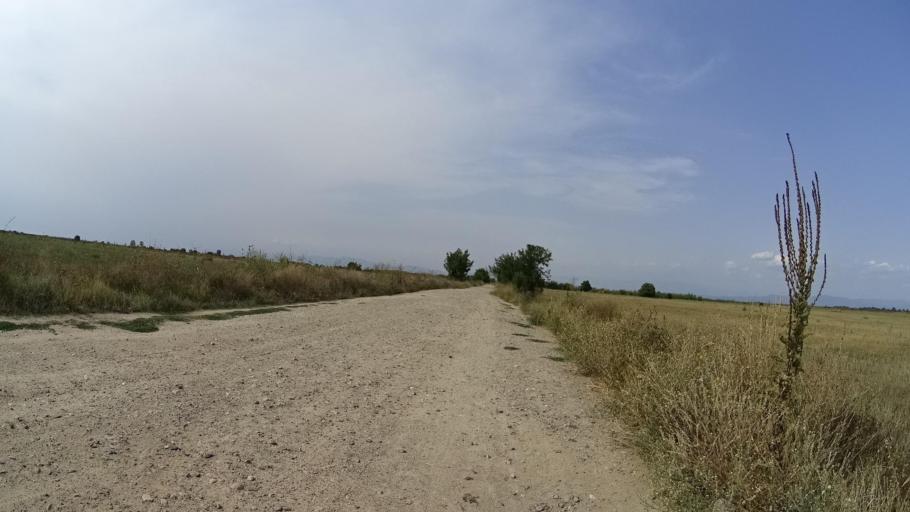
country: BG
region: Plovdiv
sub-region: Obshtina Kaloyanovo
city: Kaloyanovo
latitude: 42.2744
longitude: 24.8009
